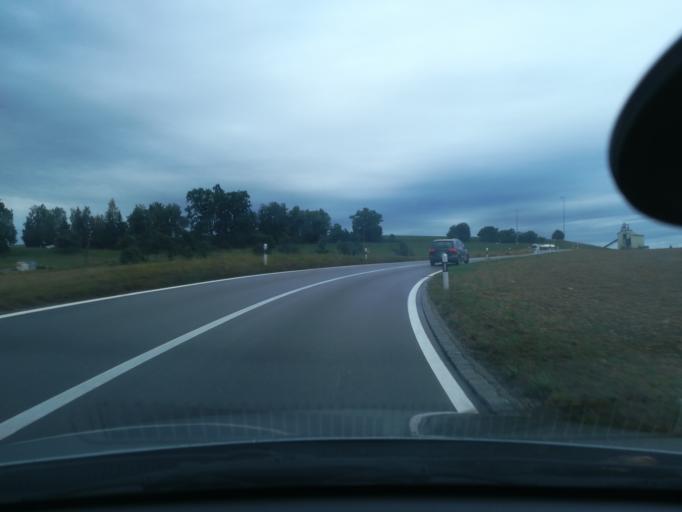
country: CH
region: Thurgau
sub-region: Frauenfeld District
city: Huttwilen
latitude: 47.5976
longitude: 8.8914
